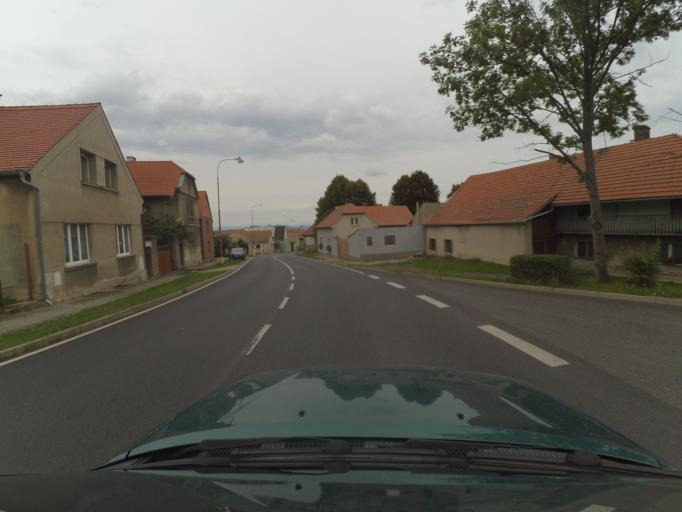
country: CZ
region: Ustecky
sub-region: Okres Louny
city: Louny
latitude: 50.3111
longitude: 13.7994
